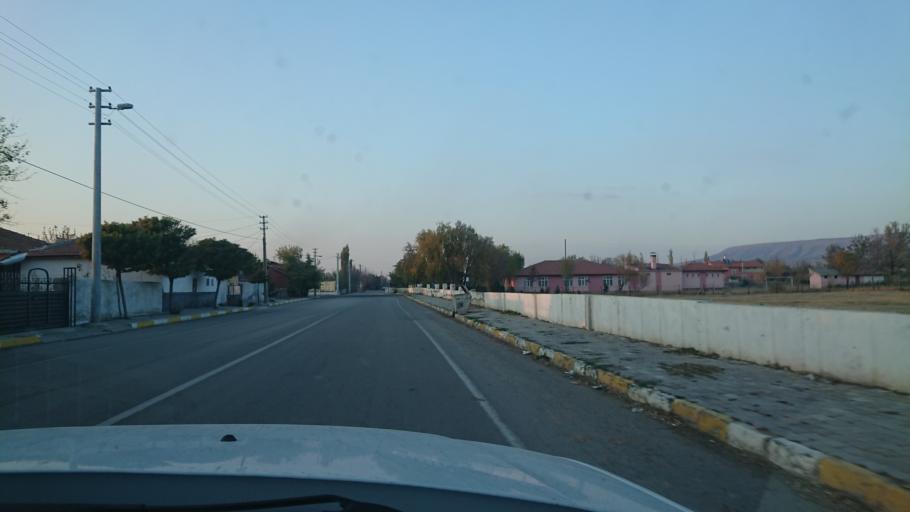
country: TR
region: Aksaray
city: Aksaray
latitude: 38.3002
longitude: 34.0726
